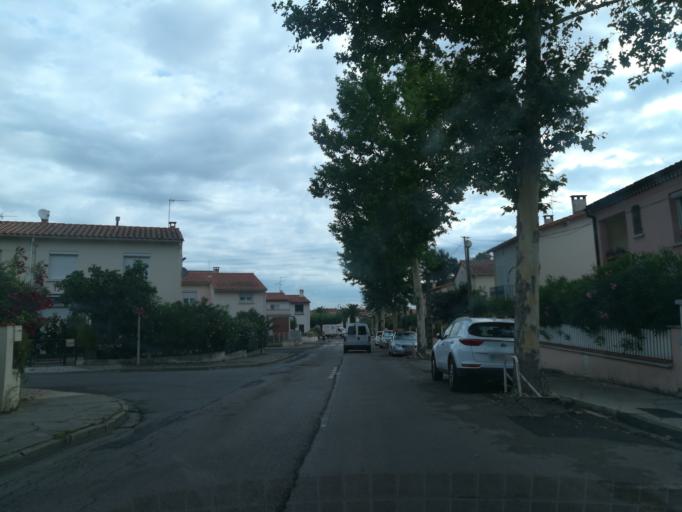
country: FR
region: Languedoc-Roussillon
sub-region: Departement des Pyrenees-Orientales
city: Ceret
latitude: 42.4877
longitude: 2.7512
